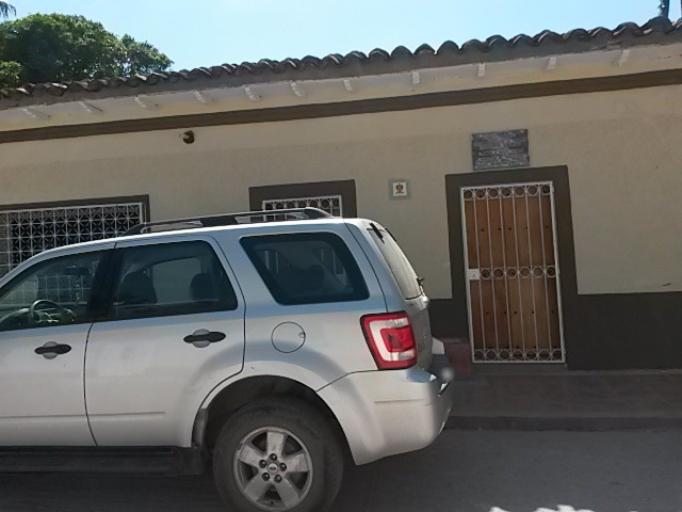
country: MX
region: Oaxaca
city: Asuncion Ixtaltepec
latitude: 16.5045
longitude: -95.0564
